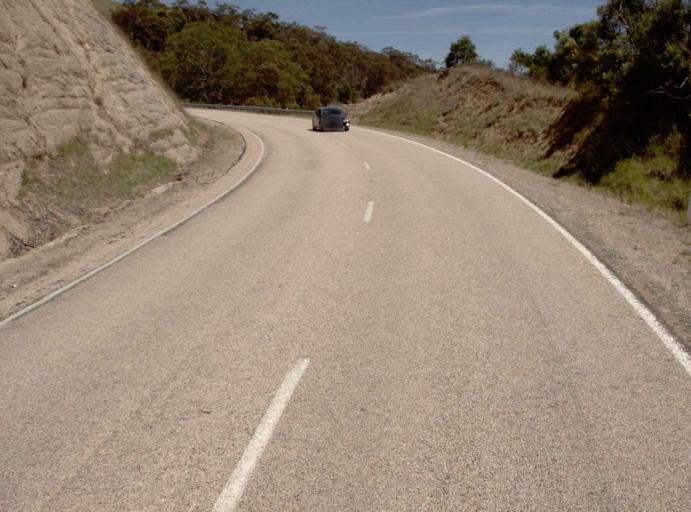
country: AU
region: Victoria
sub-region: Alpine
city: Mount Beauty
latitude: -37.1612
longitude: 147.6575
